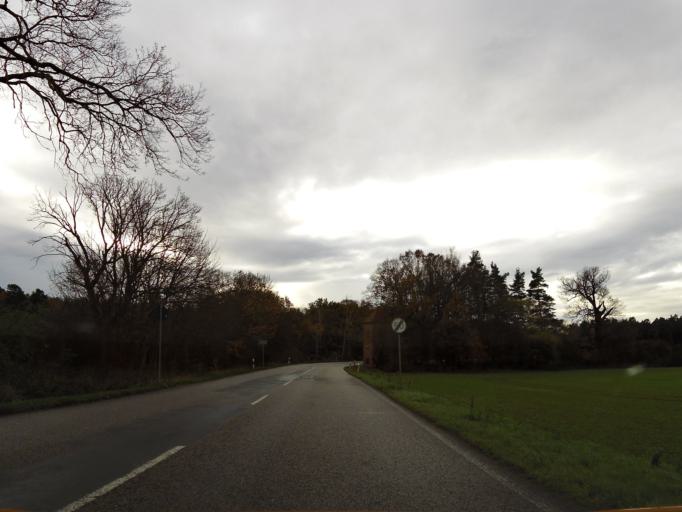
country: DE
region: Saxony-Anhalt
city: Haldensleben I
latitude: 52.3531
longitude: 11.4648
